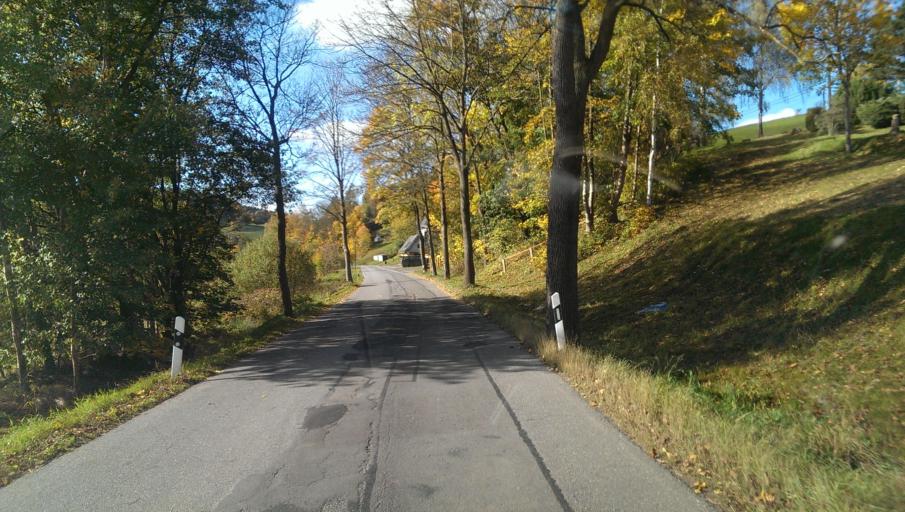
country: DE
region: Saxony
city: Rechenberg-Bienenmuhle
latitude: 50.7355
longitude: 13.5681
